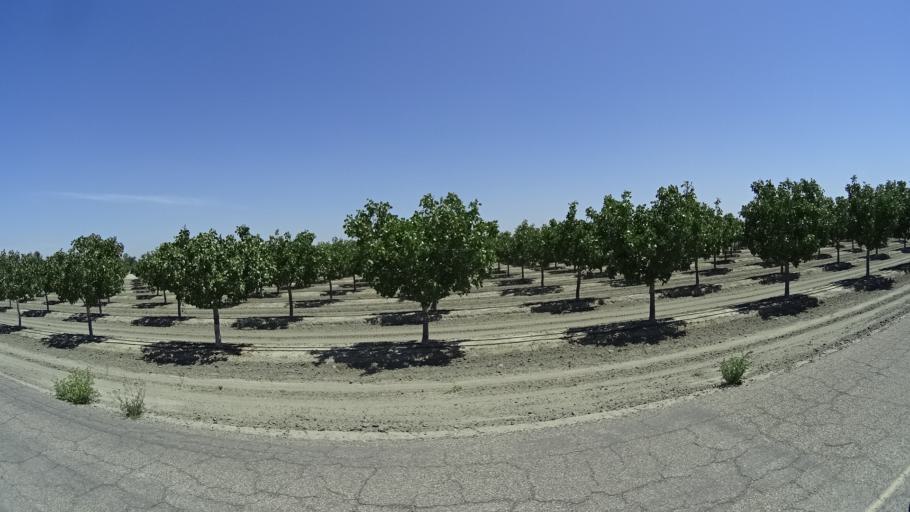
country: US
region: California
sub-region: Kings County
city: Corcoran
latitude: 36.1050
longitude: -119.5990
